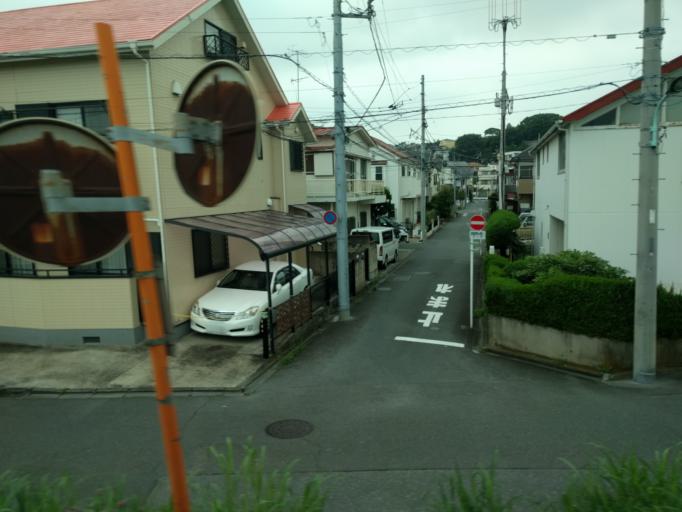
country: JP
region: Kanagawa
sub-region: Kawasaki-shi
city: Kawasaki
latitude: 35.5922
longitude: 139.6590
